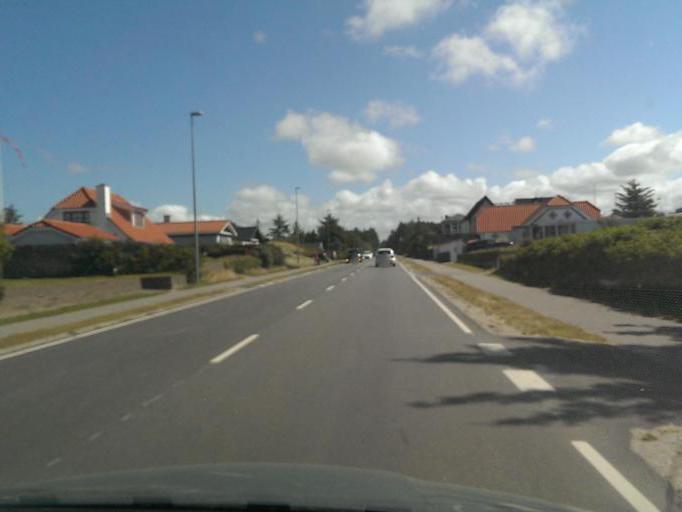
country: DK
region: North Denmark
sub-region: Jammerbugt Kommune
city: Pandrup
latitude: 57.2510
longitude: 9.5914
